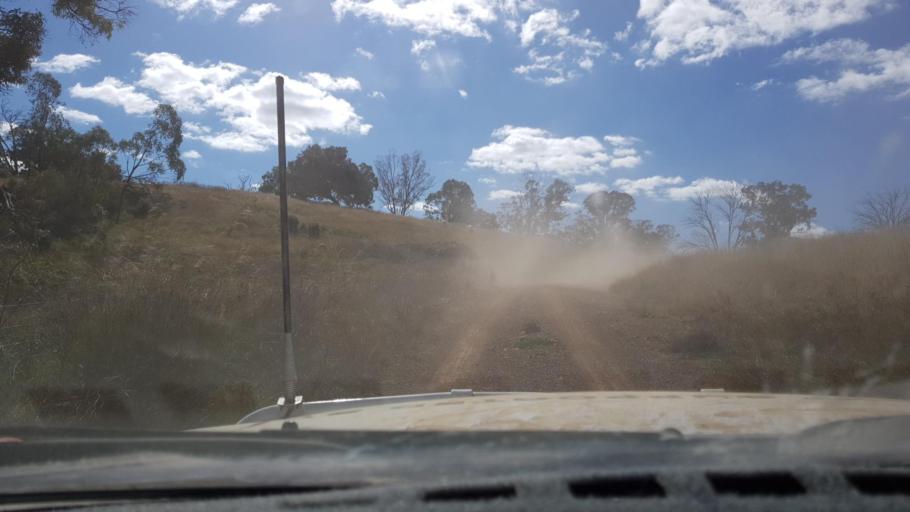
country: AU
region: New South Wales
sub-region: Tamworth Municipality
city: Manilla
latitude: -30.4393
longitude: 150.8382
